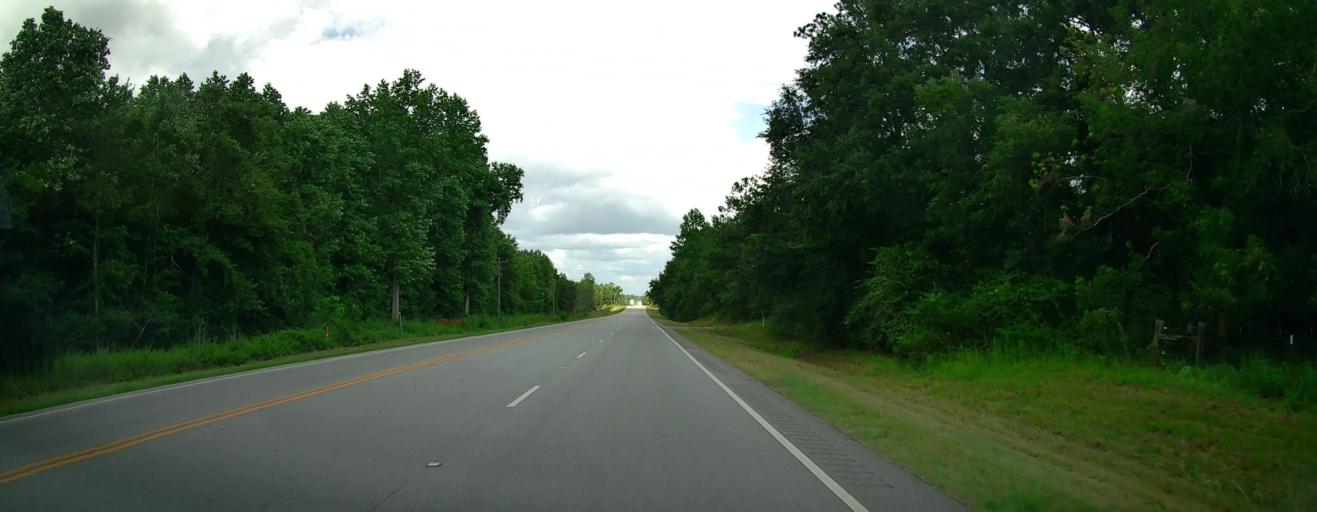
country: US
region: Georgia
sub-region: Coffee County
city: Broxton
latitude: 31.5666
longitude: -83.0075
